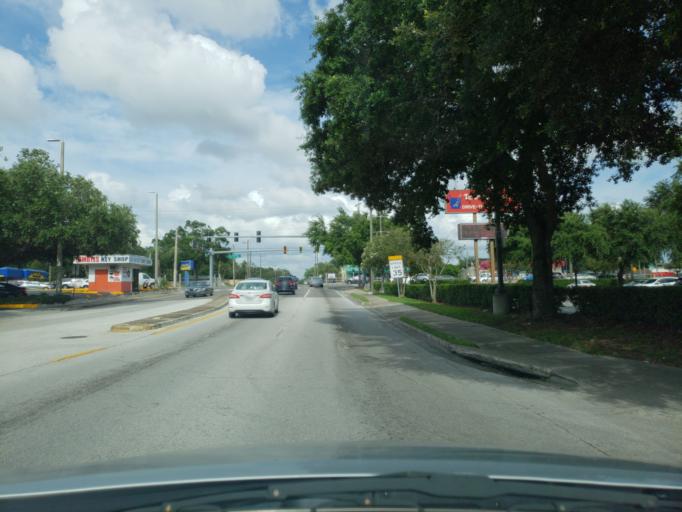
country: US
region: Florida
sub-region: Hillsborough County
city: Egypt Lake-Leto
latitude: 28.0107
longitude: -82.4853
